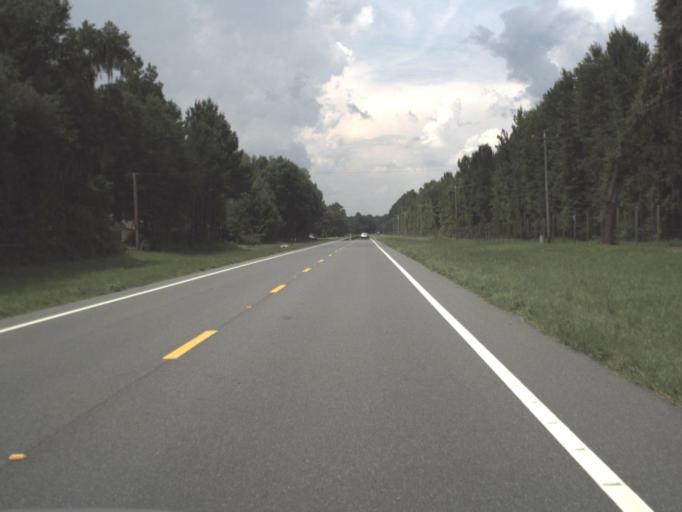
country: US
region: Florida
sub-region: Alachua County
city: Alachua
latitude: 29.8451
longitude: -82.3472
